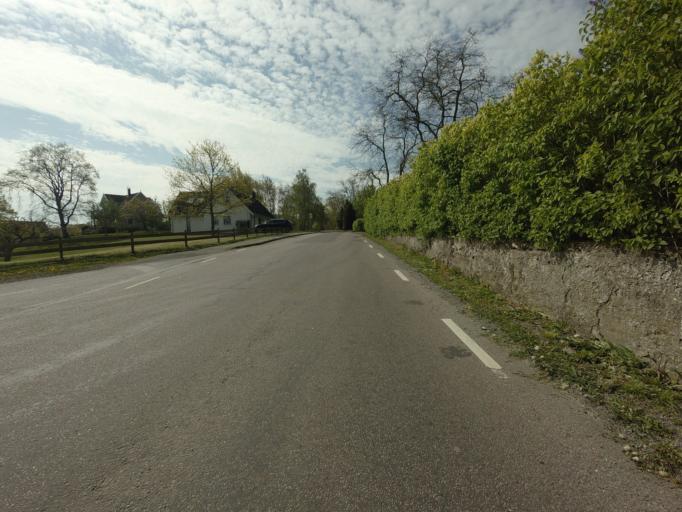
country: SE
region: Skane
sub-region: Hoganas Kommun
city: Hoganas
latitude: 56.2707
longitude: 12.5784
